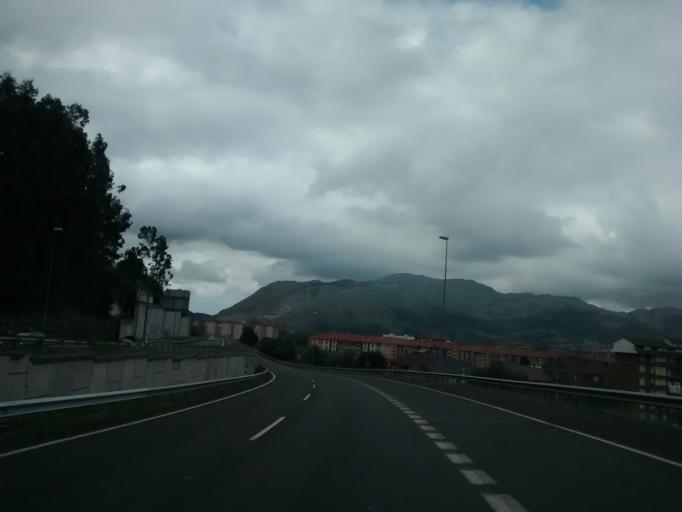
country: ES
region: Cantabria
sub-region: Provincia de Cantabria
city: Los Corrales de Buelna
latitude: 43.2540
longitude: -4.0723
